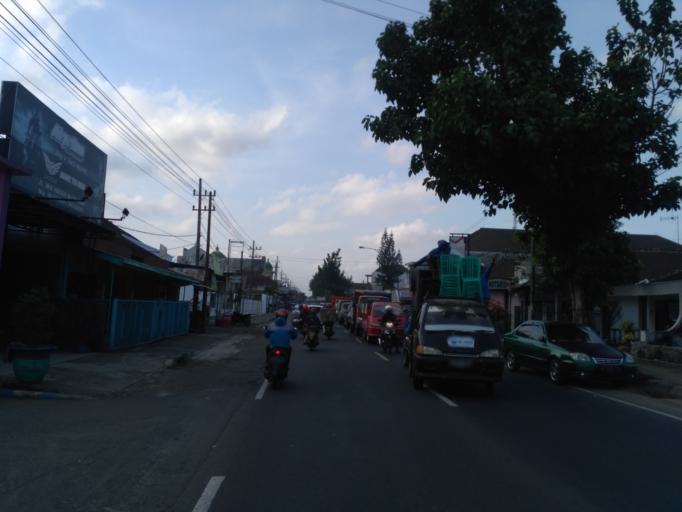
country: ID
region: East Java
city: Pakisaji
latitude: -8.0672
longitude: 112.5981
